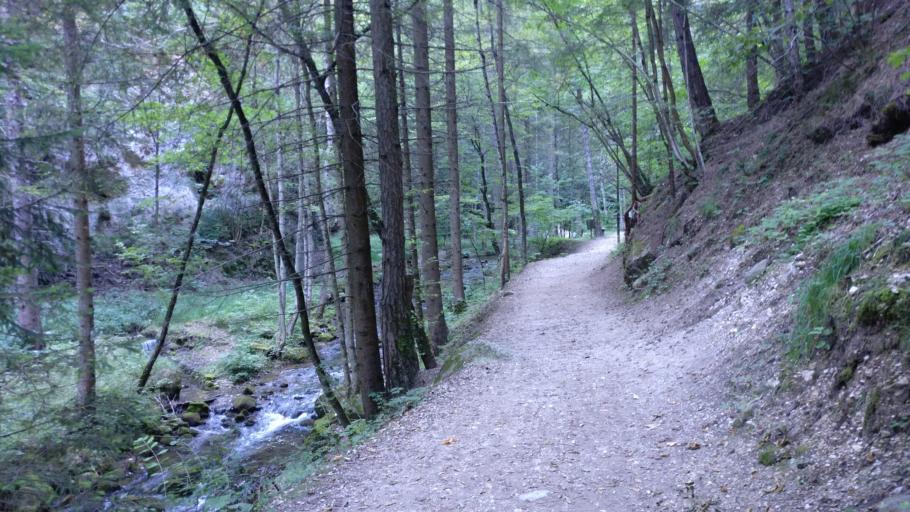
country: IT
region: Trentino-Alto Adige
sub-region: Provincia di Trento
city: Fondo
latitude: 46.4424
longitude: 11.1416
